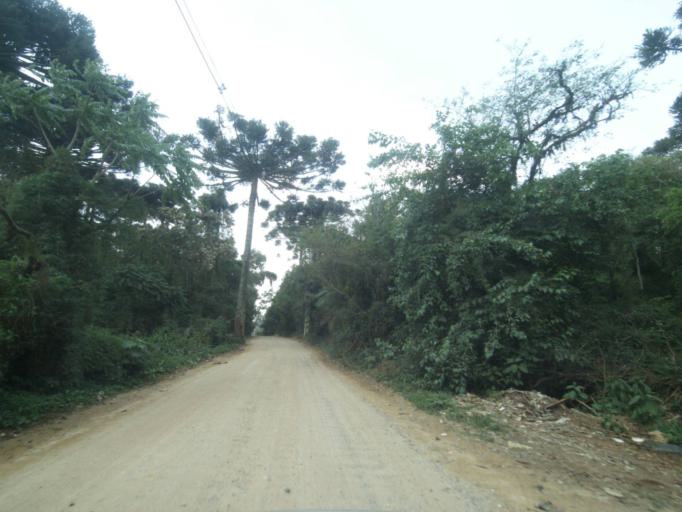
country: BR
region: Parana
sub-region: Sao Jose Dos Pinhais
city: Sao Jose dos Pinhais
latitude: -25.5428
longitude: -49.2348
